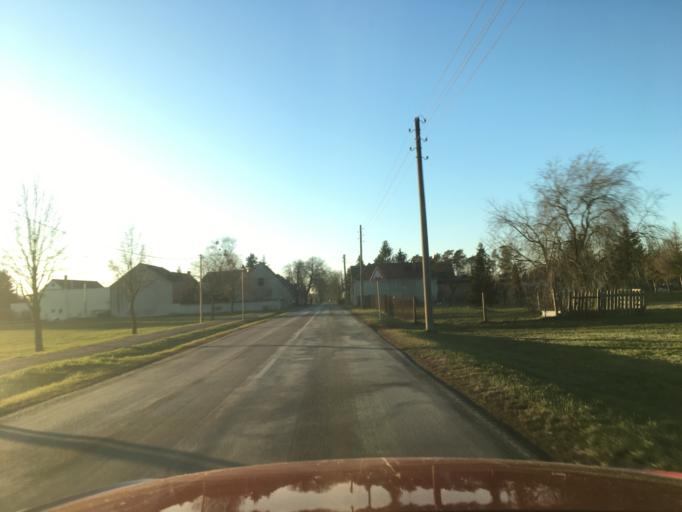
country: DE
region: Saxony-Anhalt
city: Klieken
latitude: 51.9242
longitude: 12.3189
